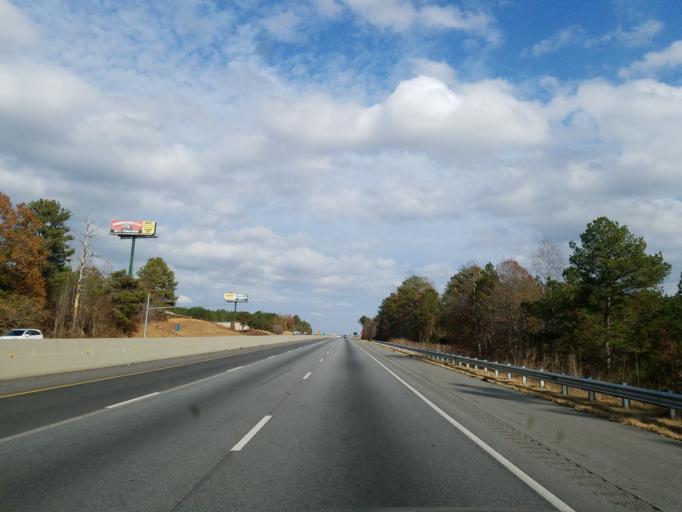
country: US
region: Alabama
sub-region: Cleburne County
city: Heflin
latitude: 33.6481
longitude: -85.4253
